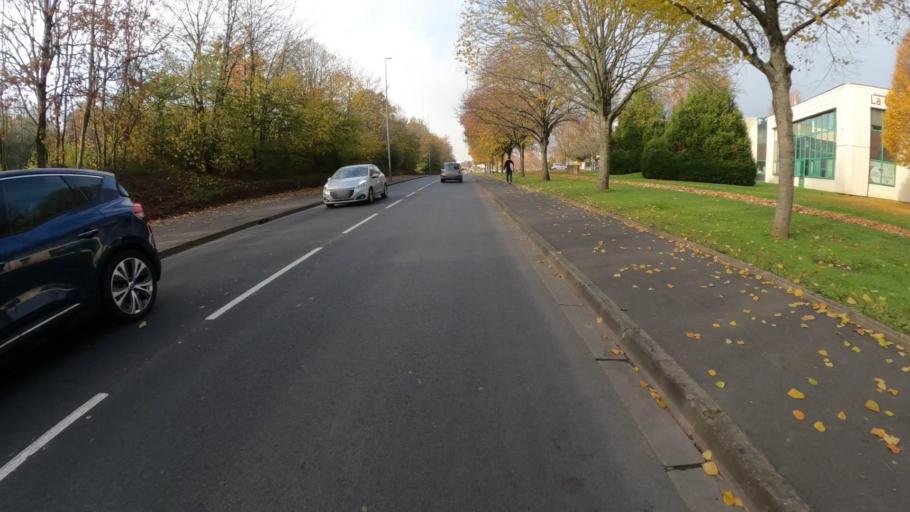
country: FR
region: Lower Normandy
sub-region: Departement du Calvados
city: Saint-Contest
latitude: 49.1993
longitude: -0.3914
